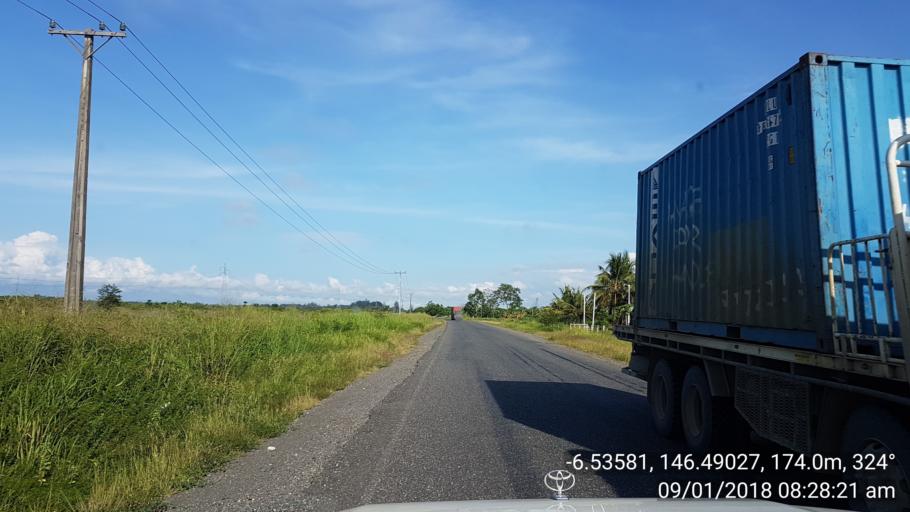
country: PG
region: Morobe
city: Lae
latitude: -6.5359
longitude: 146.4905
